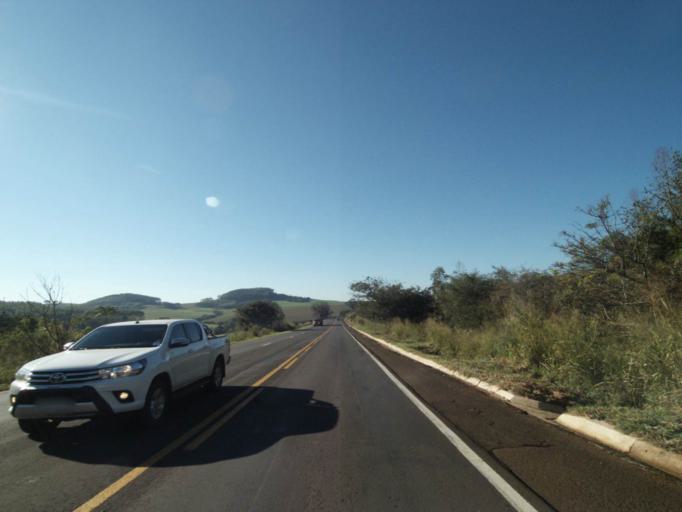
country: BR
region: Parana
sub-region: Londrina
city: Londrina
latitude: -23.5395
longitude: -51.1295
